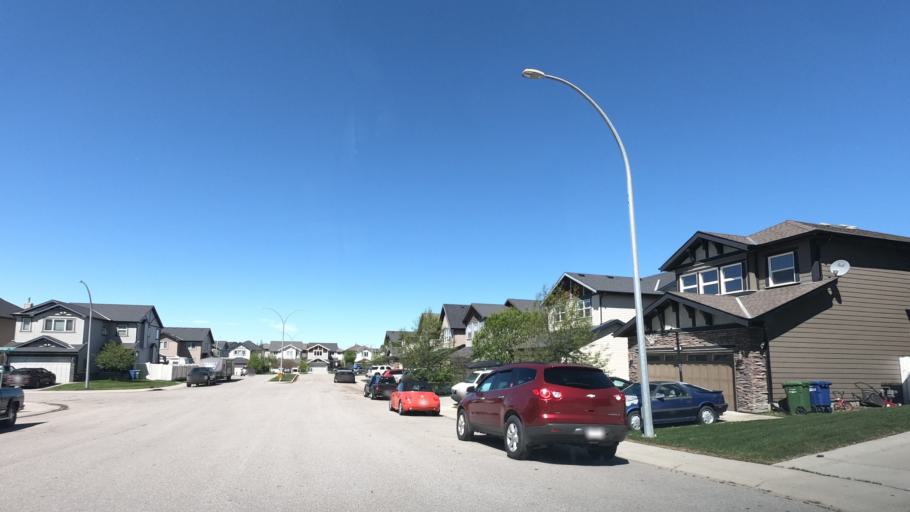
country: CA
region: Alberta
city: Airdrie
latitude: 51.2649
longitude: -113.9830
